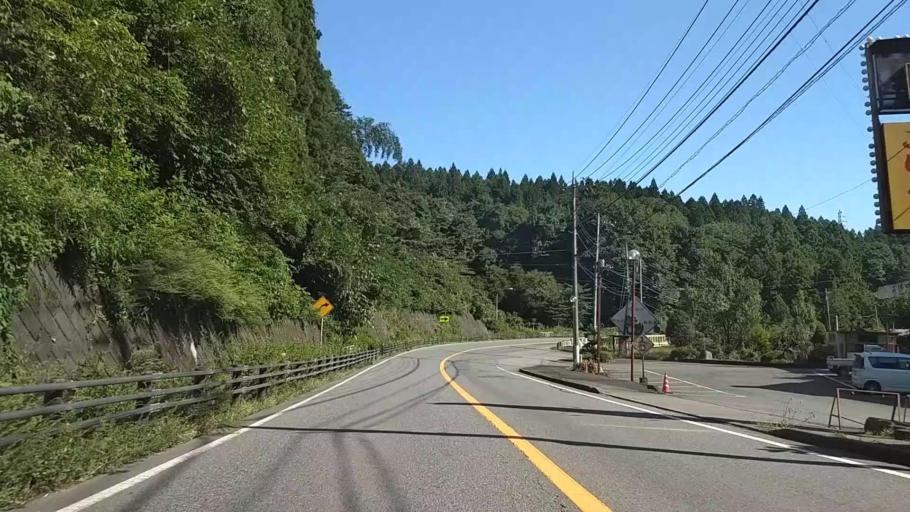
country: JP
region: Gunma
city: Annaka
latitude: 36.3349
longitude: 138.7174
